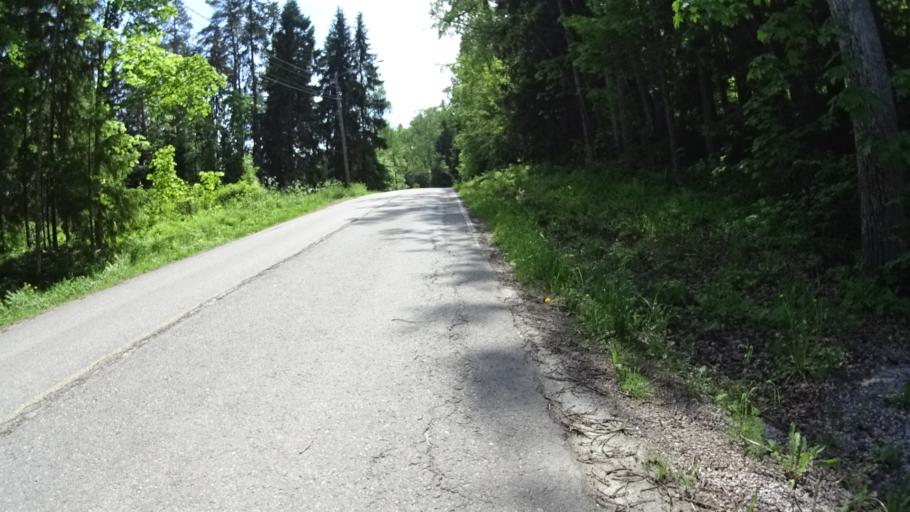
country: FI
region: Uusimaa
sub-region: Helsinki
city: Espoo
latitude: 60.2584
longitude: 24.6523
